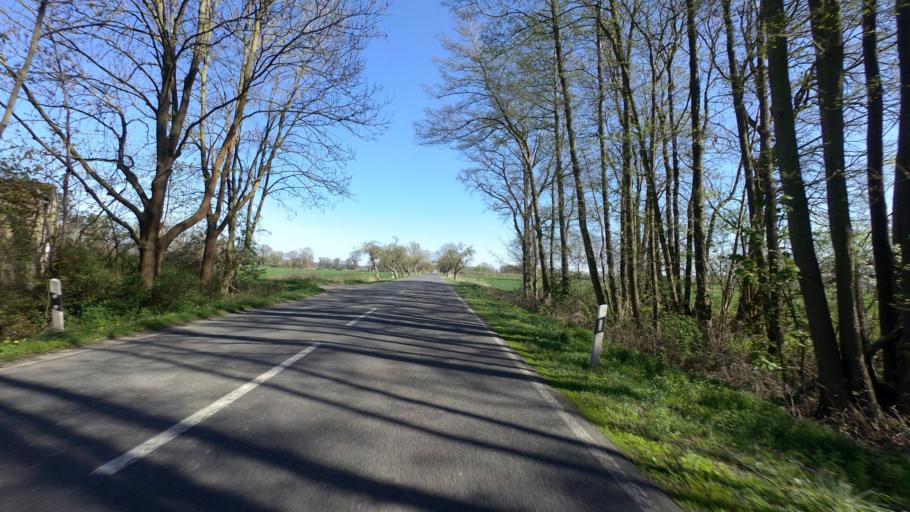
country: DE
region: Saxony-Anhalt
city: Kalbe
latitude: 52.6526
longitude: 11.4044
